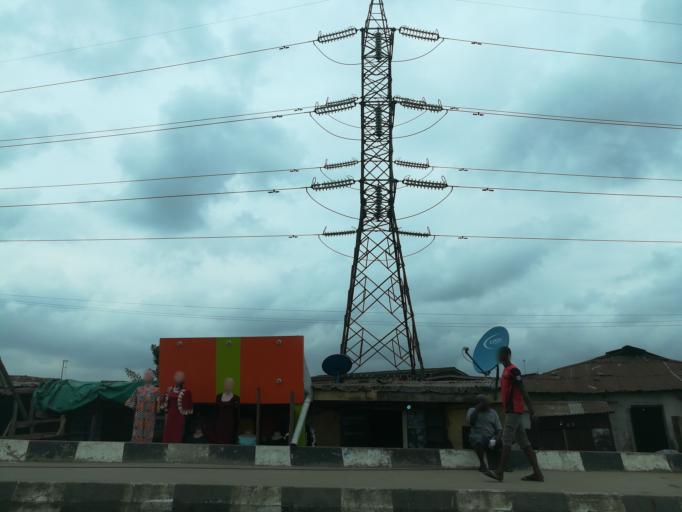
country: NG
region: Lagos
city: Ojota
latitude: 6.6041
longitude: 3.4021
